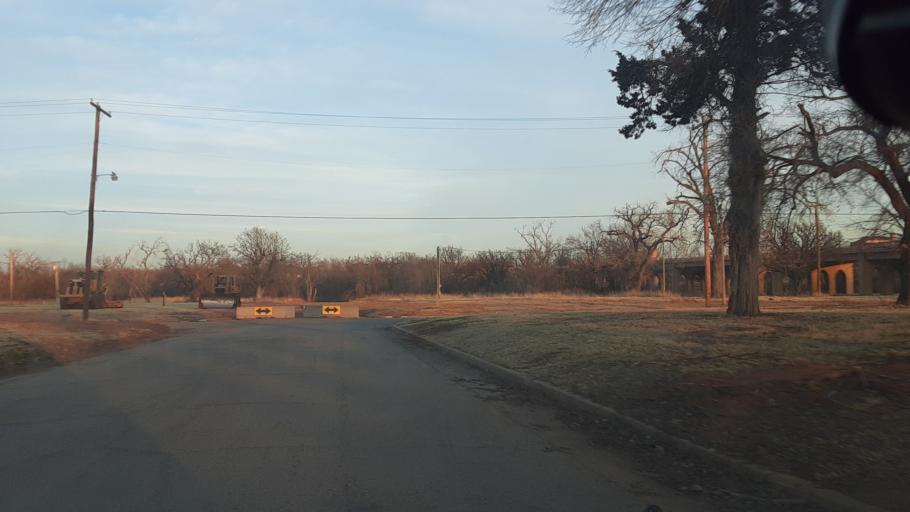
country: US
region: Oklahoma
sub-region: Logan County
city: Guthrie
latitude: 35.8811
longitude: -97.4320
